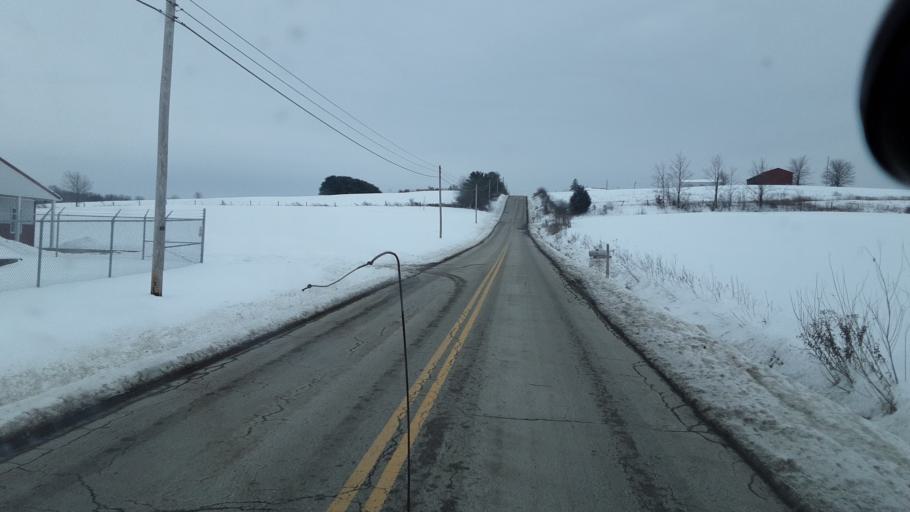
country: US
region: Ohio
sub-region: Perry County
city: Somerset
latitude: 39.9337
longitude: -82.2236
